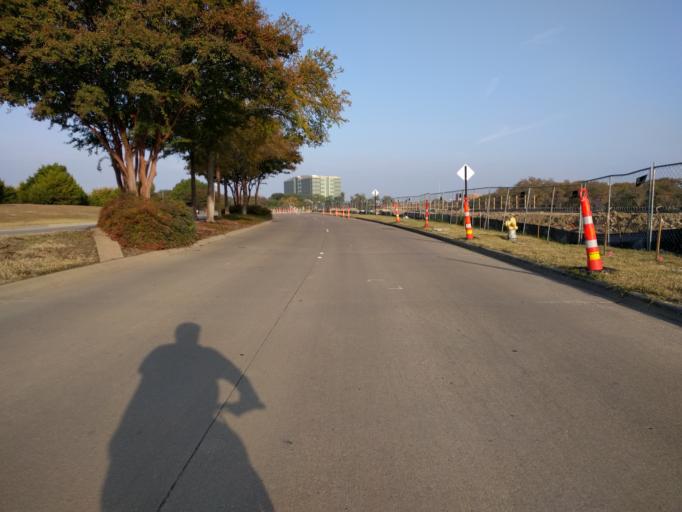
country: US
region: Texas
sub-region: Collin County
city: Plano
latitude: 32.9894
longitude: -96.7045
